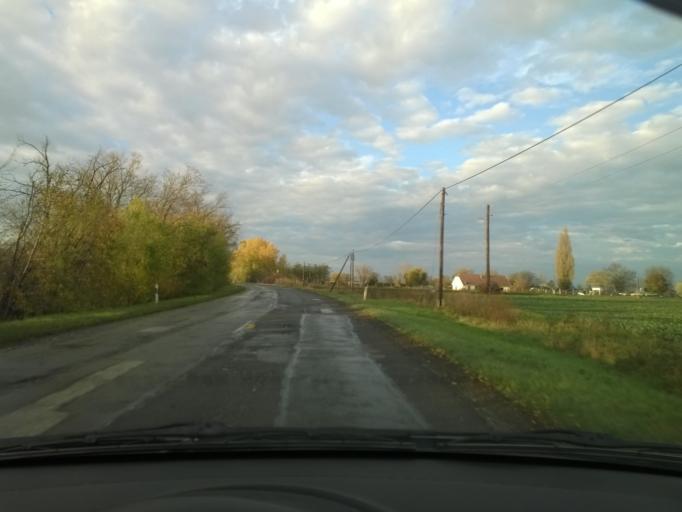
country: HU
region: Bacs-Kiskun
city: Kalocsa
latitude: 46.5429
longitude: 18.9856
